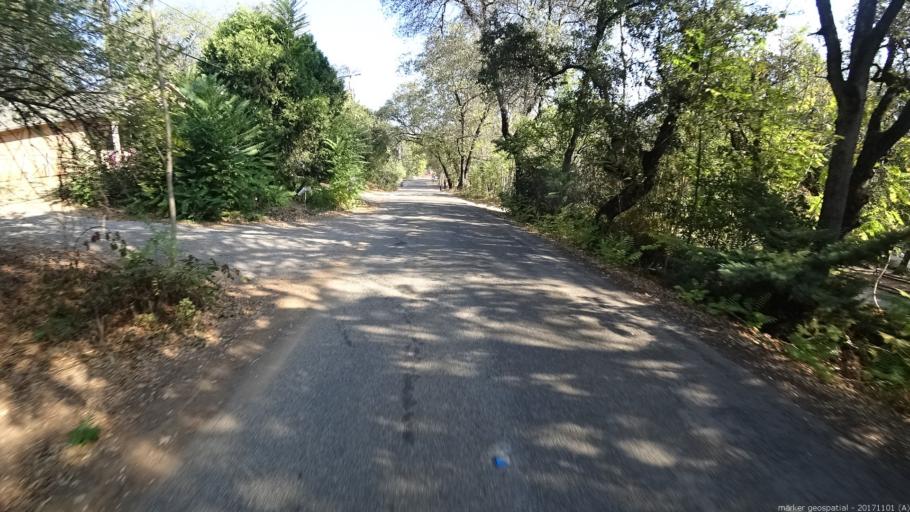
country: US
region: California
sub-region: Shasta County
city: Shasta Lake
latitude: 40.7142
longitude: -122.3347
